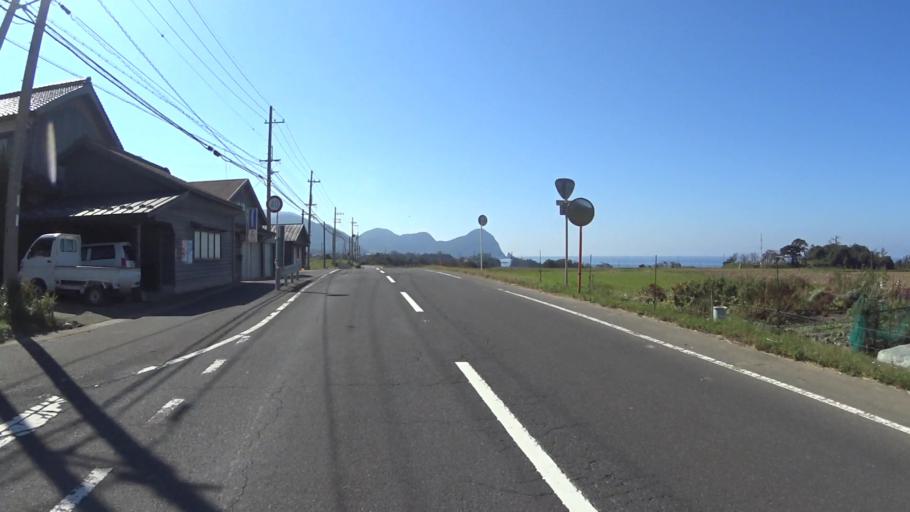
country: JP
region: Kyoto
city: Miyazu
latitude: 35.7642
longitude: 135.1895
